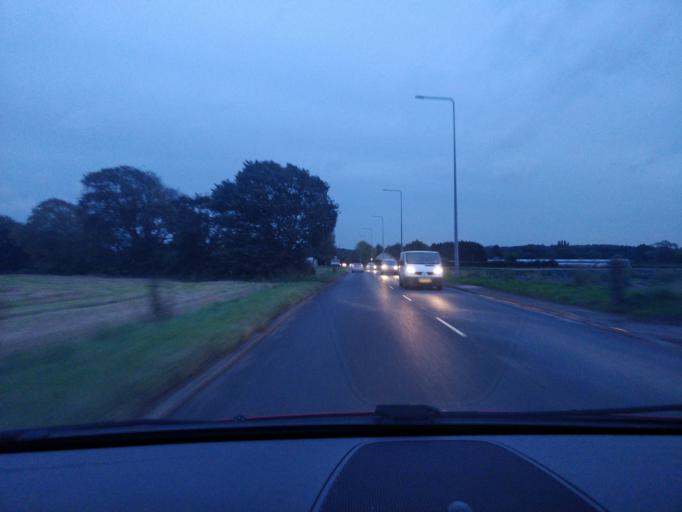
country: GB
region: England
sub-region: Lancashire
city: Ormskirk
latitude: 53.5920
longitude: -2.9197
